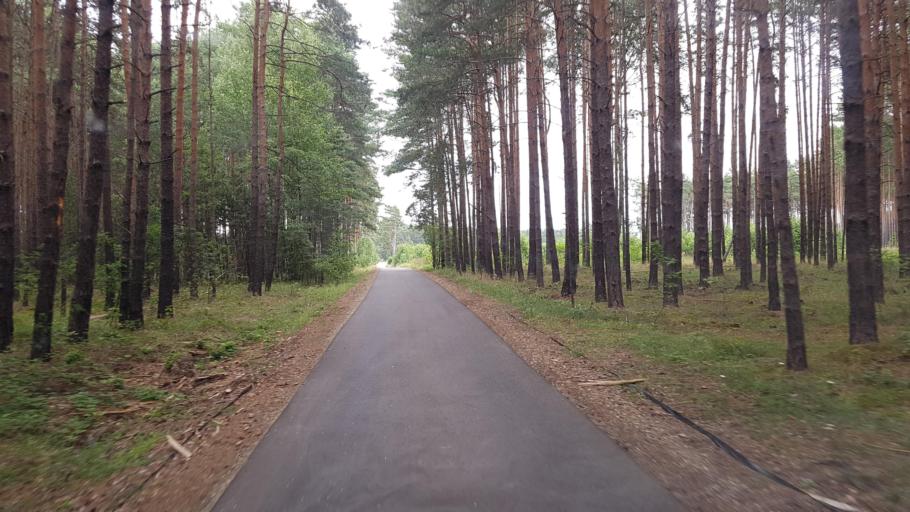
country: DE
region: Brandenburg
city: Grossraschen
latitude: 51.6044
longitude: 14.0394
